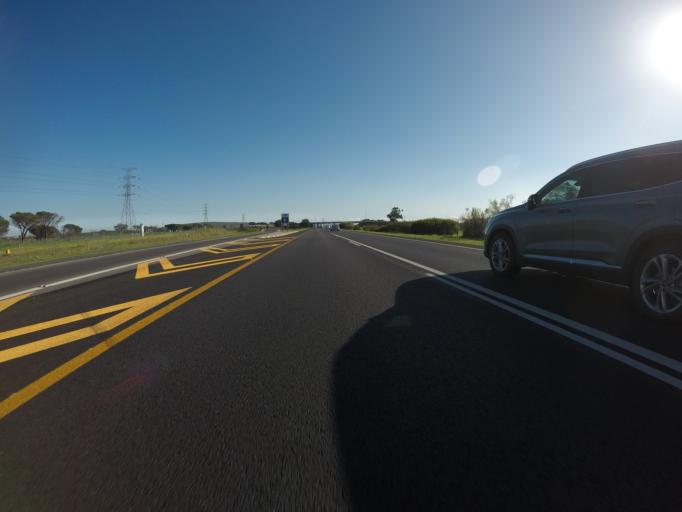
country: ZA
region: Western Cape
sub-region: Cape Winelands District Municipality
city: Stellenbosch
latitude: -34.0591
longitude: 18.7853
